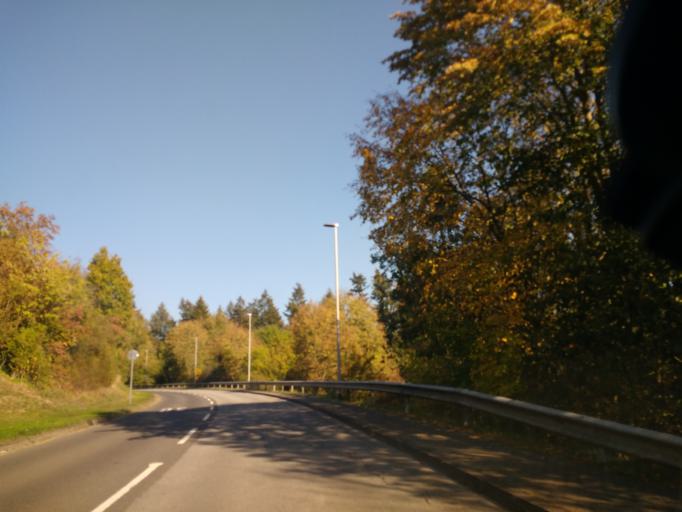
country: DE
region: Rheinland-Pfalz
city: Konz
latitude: 49.6971
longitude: 6.5906
